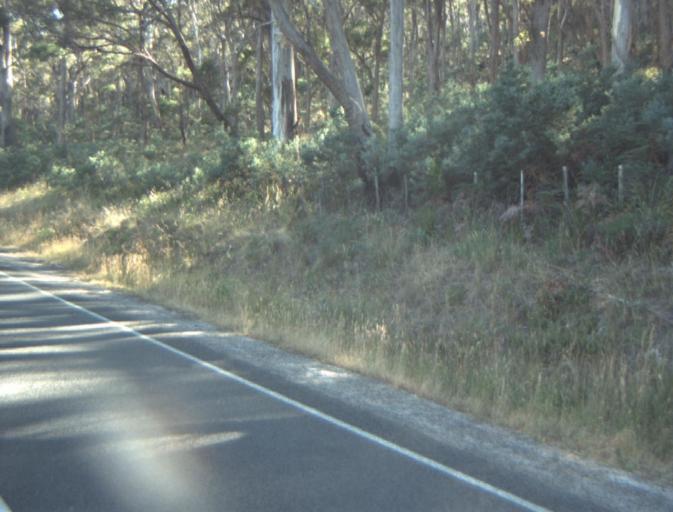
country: AU
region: Tasmania
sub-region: Launceston
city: Newstead
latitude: -41.4234
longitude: 147.2555
